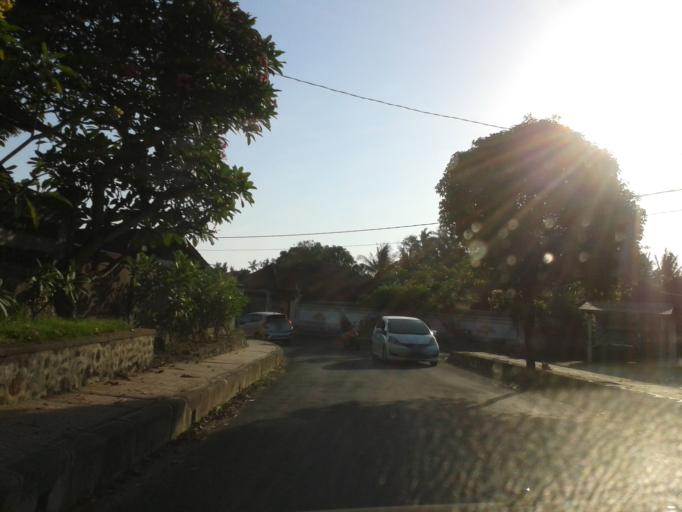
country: ID
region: Bali
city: Semarapura
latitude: -8.5640
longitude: 115.3853
